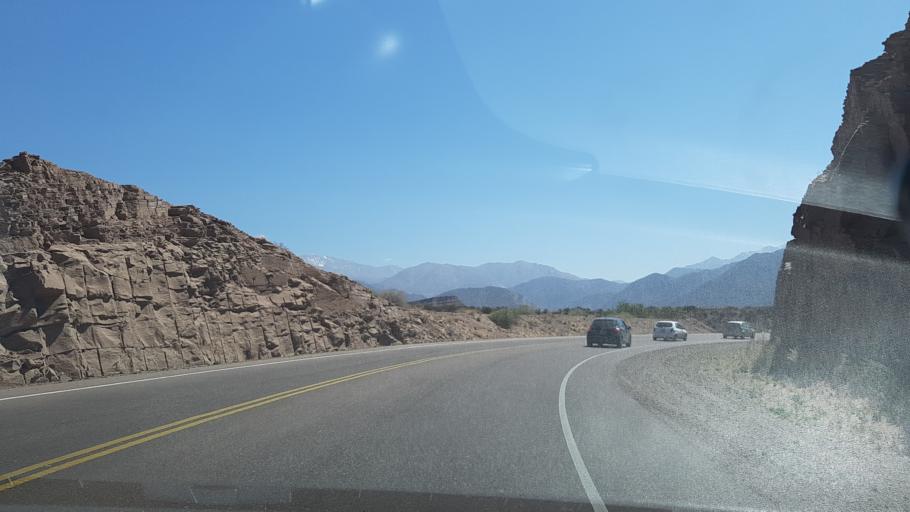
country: AR
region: Mendoza
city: Lujan de Cuyo
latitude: -32.9911
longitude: -69.1665
